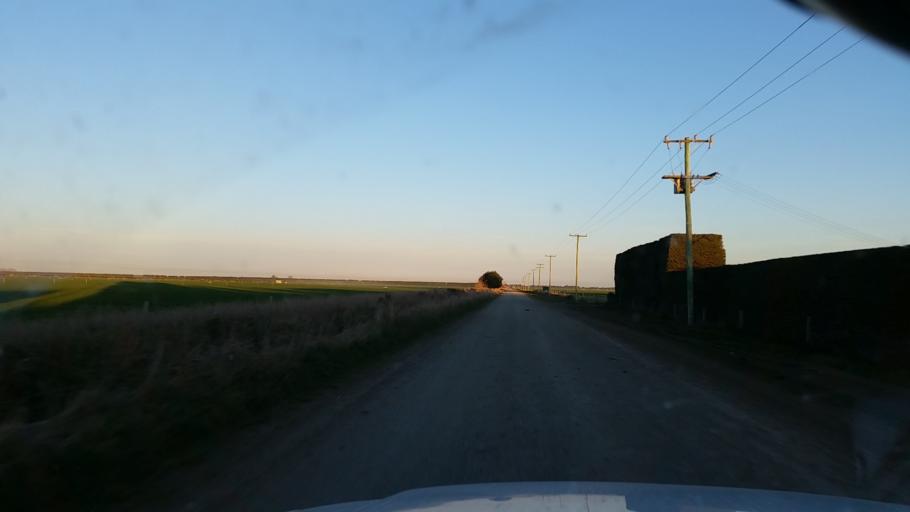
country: NZ
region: Canterbury
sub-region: Ashburton District
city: Tinwald
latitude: -43.9275
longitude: 171.5559
